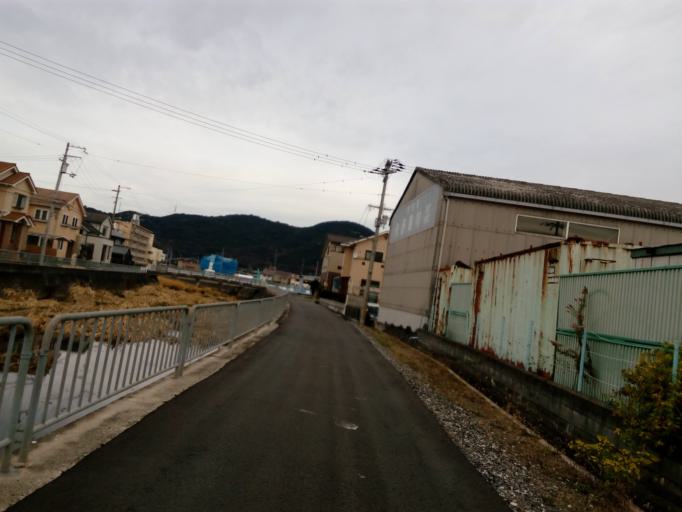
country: JP
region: Hyogo
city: Himeji
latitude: 34.8034
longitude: 134.6172
